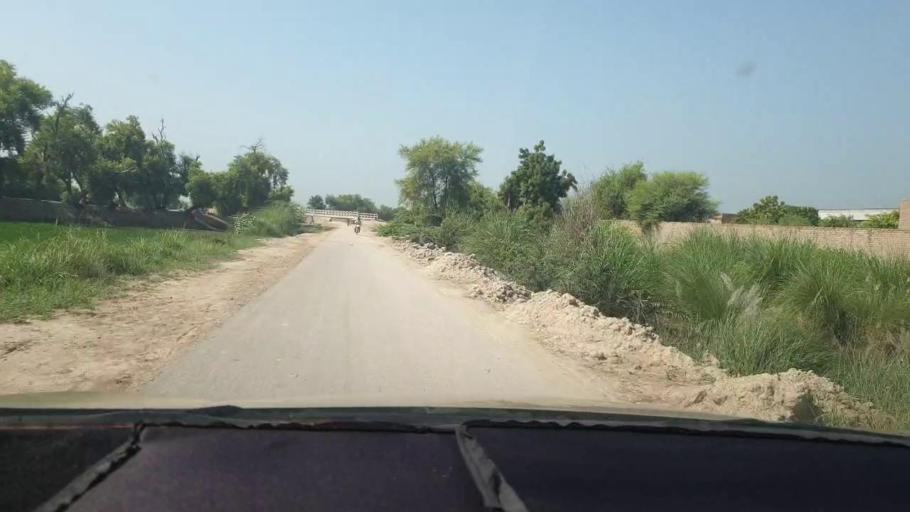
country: PK
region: Sindh
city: Kambar
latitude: 27.5781
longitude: 68.0445
